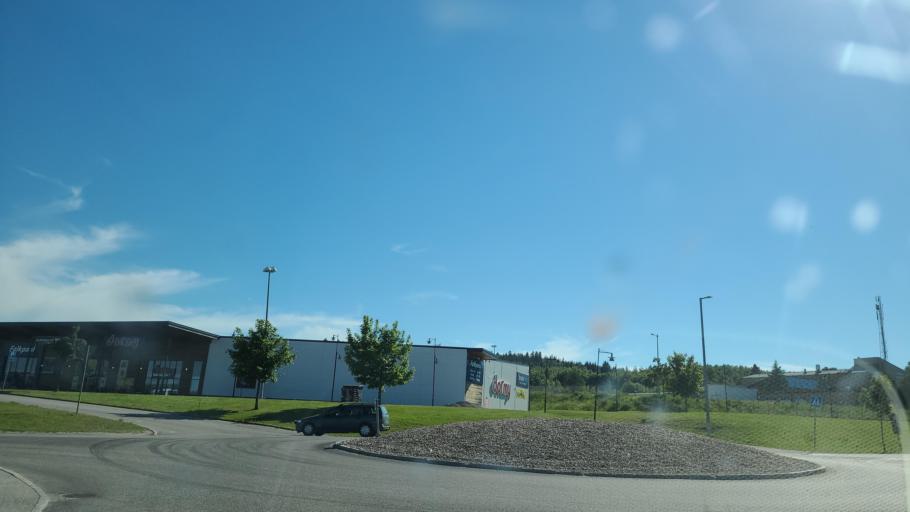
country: SE
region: Vaesternorrland
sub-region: Sundsvalls Kommun
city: Sundsbruk
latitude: 62.4420
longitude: 17.3457
